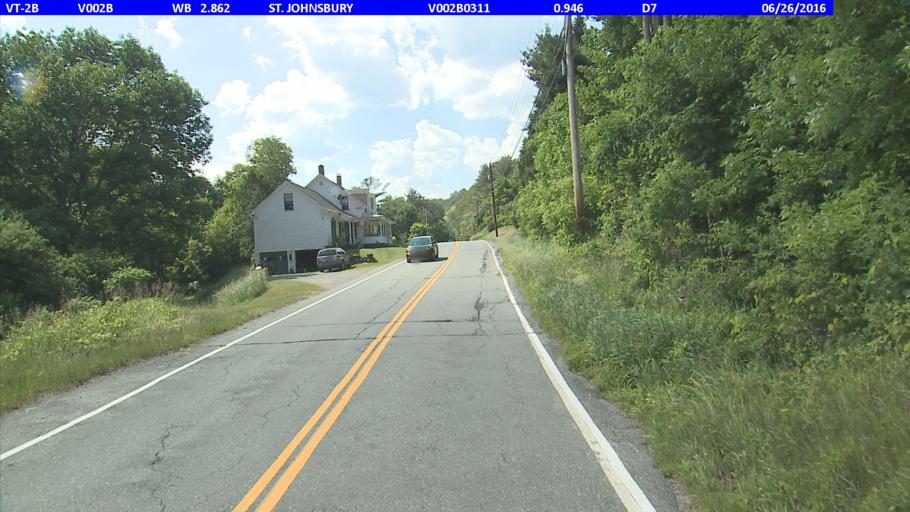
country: US
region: Vermont
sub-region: Caledonia County
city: St Johnsbury
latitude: 44.4241
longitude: -72.0395
